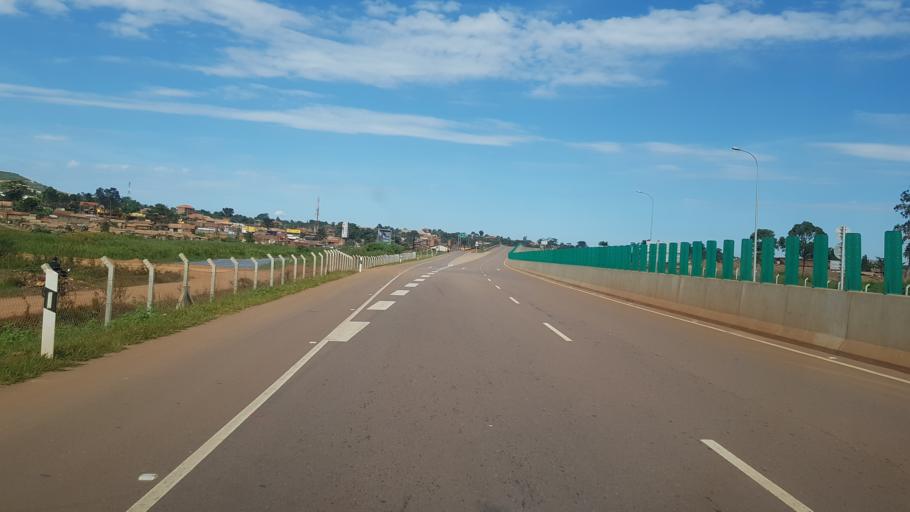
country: UG
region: Central Region
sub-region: Wakiso District
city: Kajansi
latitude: 0.2143
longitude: 32.5383
